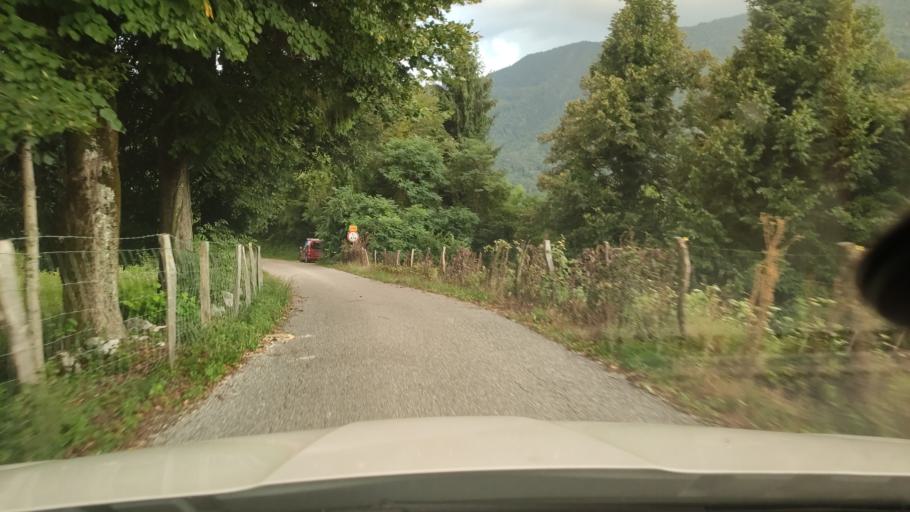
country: IT
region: Friuli Venezia Giulia
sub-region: Provincia di Udine
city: Cras
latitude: 46.2194
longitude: 13.6421
